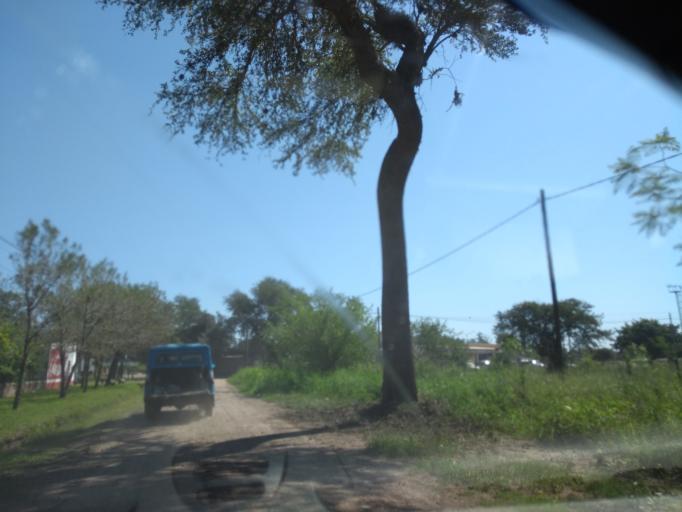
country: AR
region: Chaco
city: Resistencia
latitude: -27.4276
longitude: -58.9452
